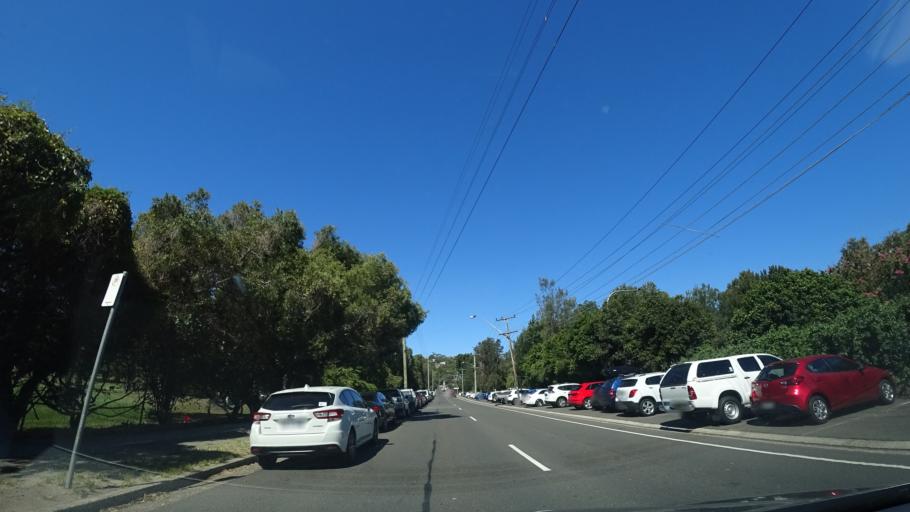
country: AU
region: New South Wales
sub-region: Warringah
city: North Manly
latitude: -33.7763
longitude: 151.2673
